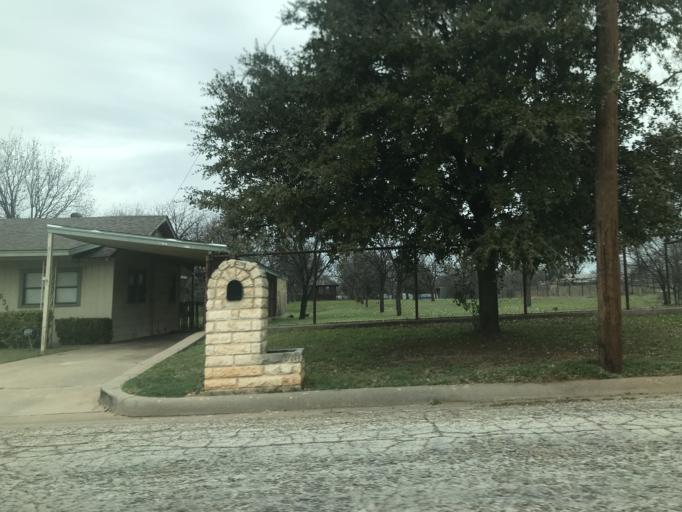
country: US
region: Texas
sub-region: Taylor County
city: Abilene
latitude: 32.4456
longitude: -99.7547
